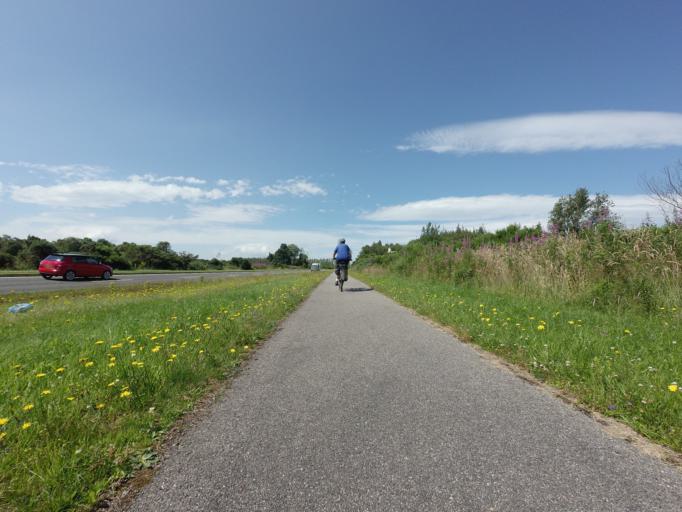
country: GB
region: Scotland
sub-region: Highland
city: Conon Bridge
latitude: 57.5388
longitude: -4.3679
